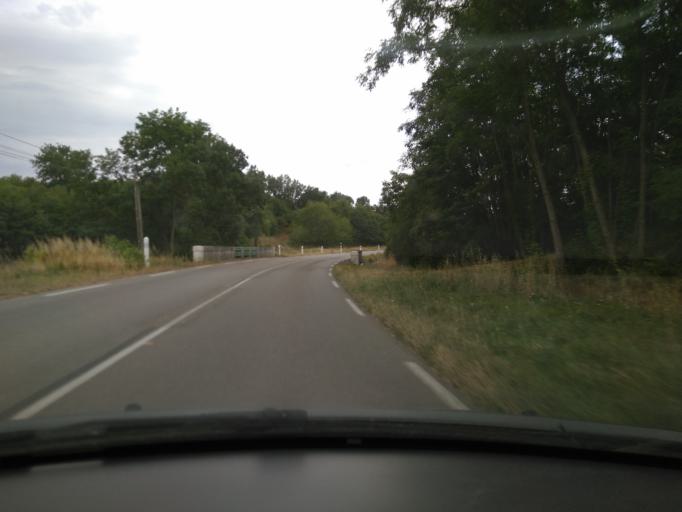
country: FR
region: Rhone-Alpes
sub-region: Departement de l'Isere
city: Beaurepaire
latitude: 45.3578
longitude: 5.0299
